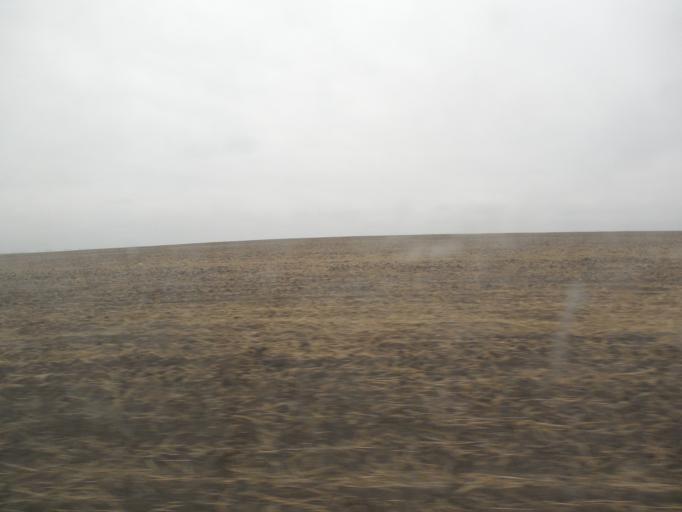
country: RU
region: Lipetsk
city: Donskoye
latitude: 52.6039
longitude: 38.9100
